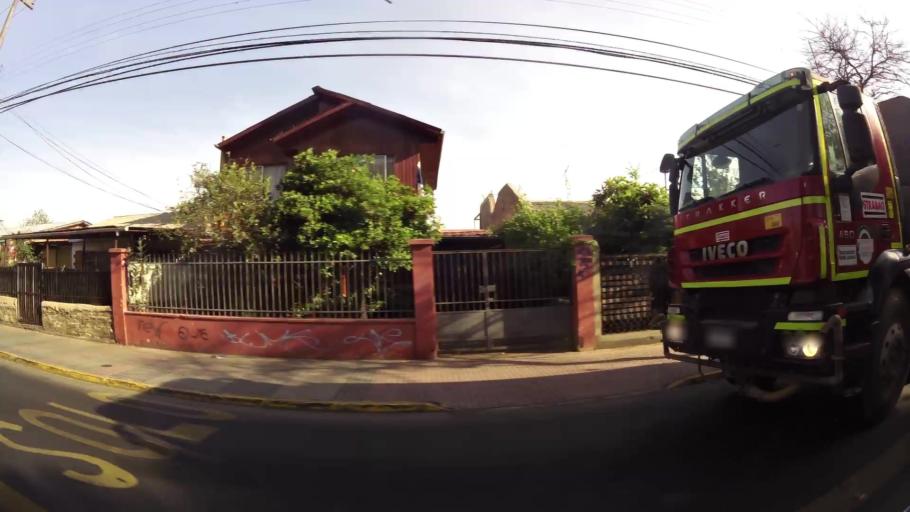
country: CL
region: Santiago Metropolitan
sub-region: Provincia de Santiago
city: Santiago
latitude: -33.5079
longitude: -70.6222
